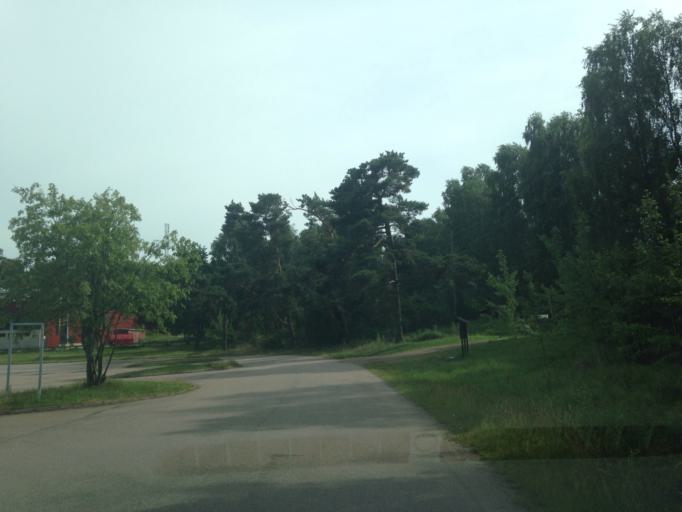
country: SE
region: Vaestra Goetaland
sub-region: Goteborg
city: Majorna
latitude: 57.7502
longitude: 11.9131
